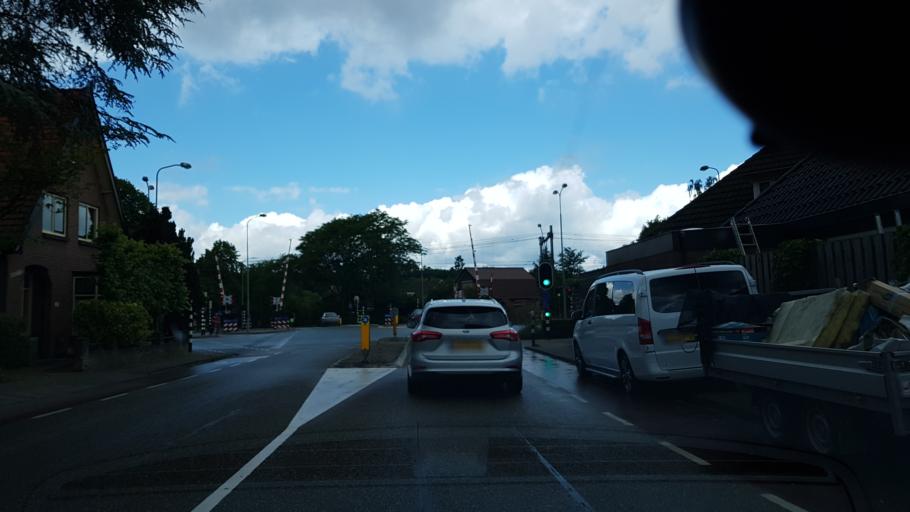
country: NL
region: Gelderland
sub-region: Gemeente Ermelo
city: Ermelo
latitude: 52.2969
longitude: 5.6121
